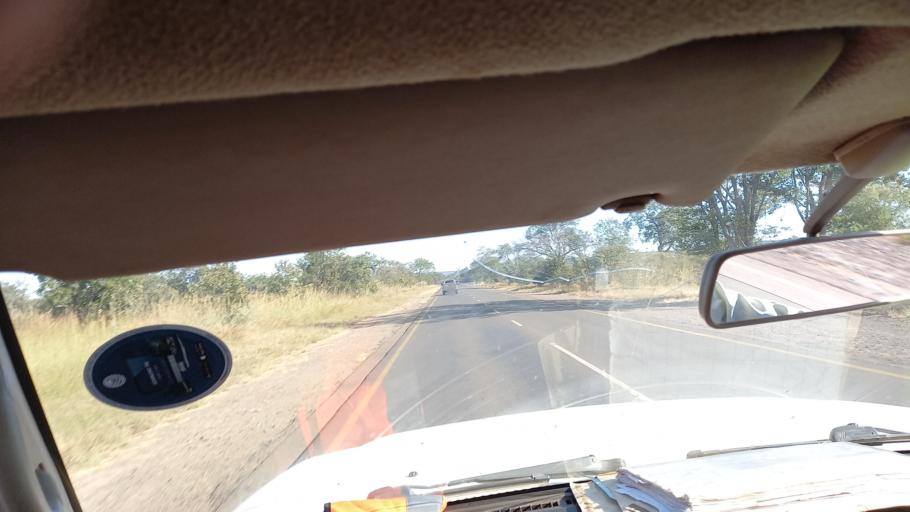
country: ZW
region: Matabeleland North
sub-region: Hwange District
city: Victoria Falls
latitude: -17.8967
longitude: 25.8569
